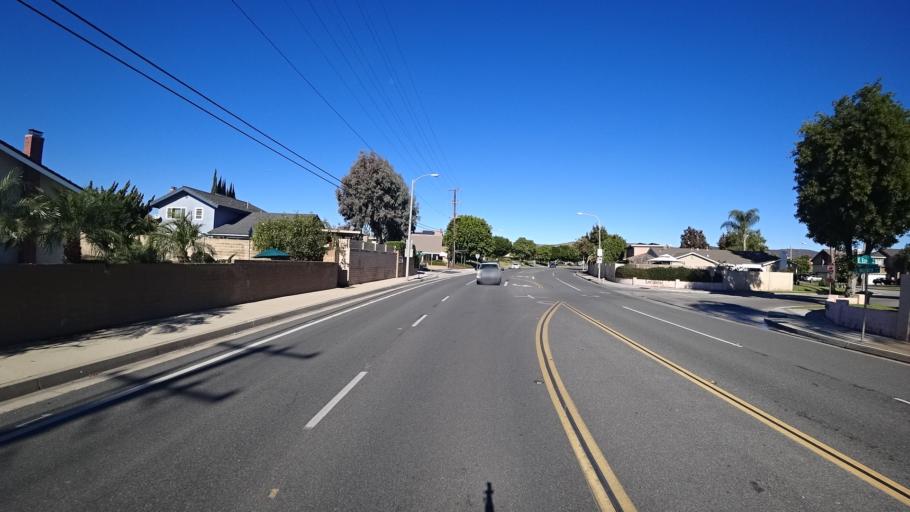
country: US
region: California
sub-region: Orange County
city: Placentia
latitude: 33.9060
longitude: -117.8551
